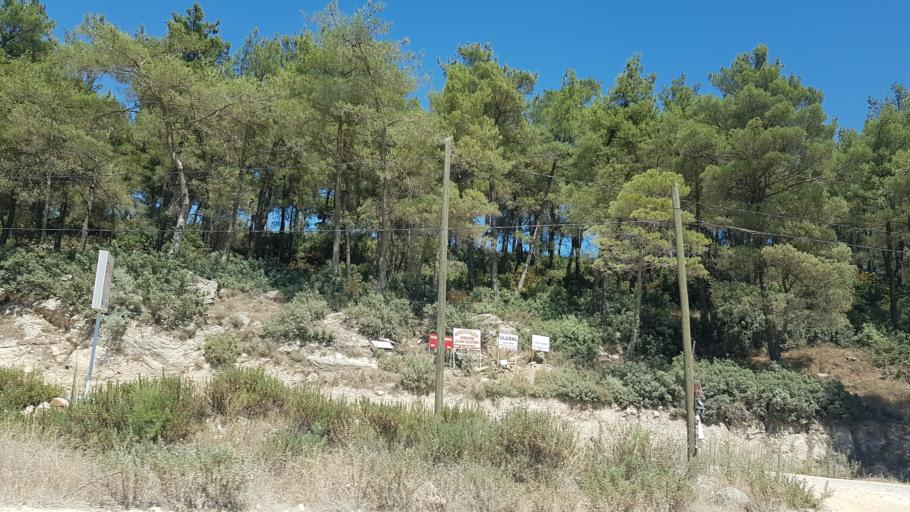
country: TR
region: Mugla
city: Turgut
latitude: 37.3070
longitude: 28.0378
